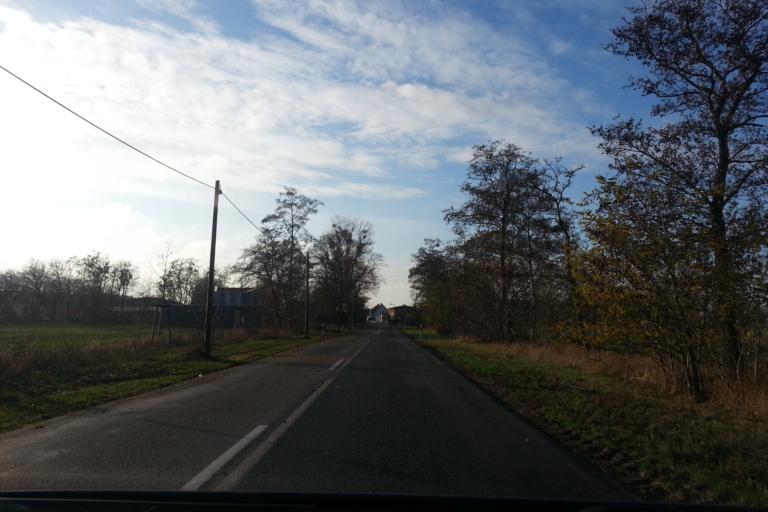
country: DE
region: Mecklenburg-Vorpommern
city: Ferdinandshof
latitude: 53.6337
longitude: 13.8259
